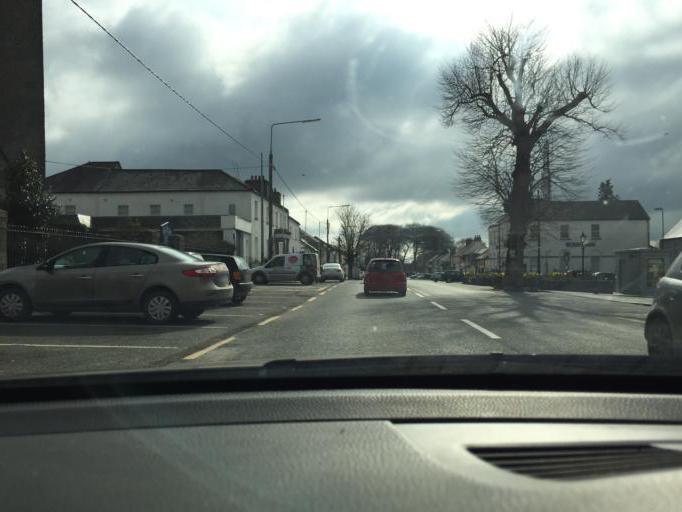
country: IE
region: Leinster
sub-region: Wicklow
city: Blessington
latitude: 53.1711
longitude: -6.5322
